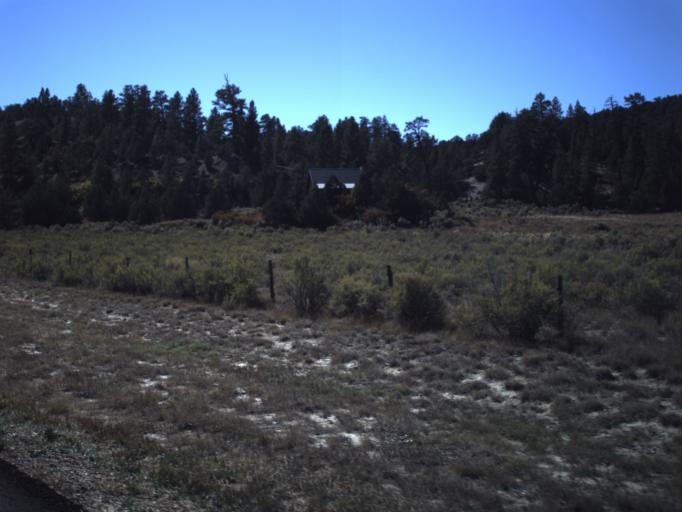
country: US
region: Utah
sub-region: Garfield County
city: Panguitch
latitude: 37.7079
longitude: -111.7885
